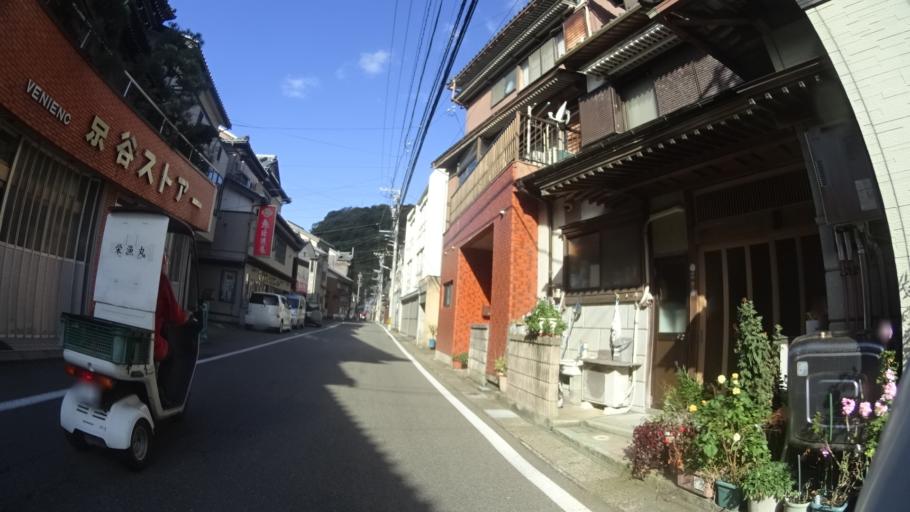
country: JP
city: Asahi
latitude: 35.9417
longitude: 135.9917
